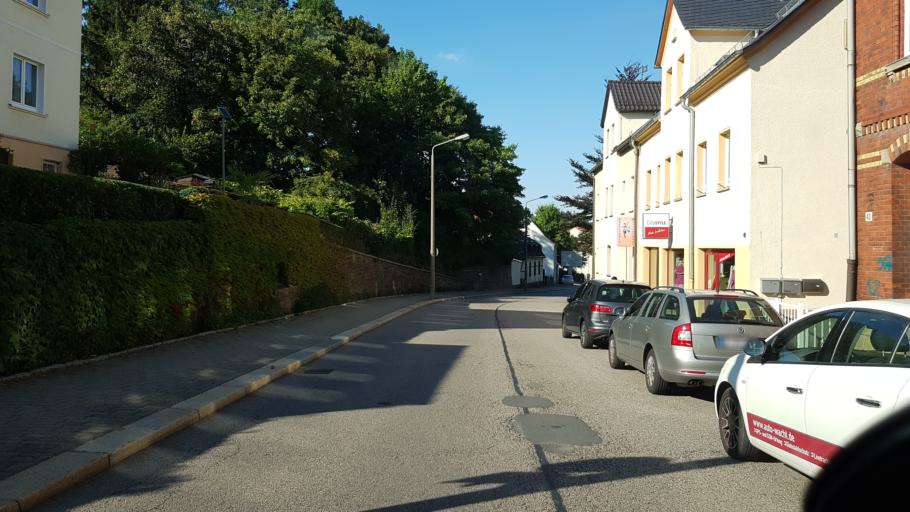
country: DE
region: Saxony
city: Wilkau-Hasslau
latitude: 50.6791
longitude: 12.4728
